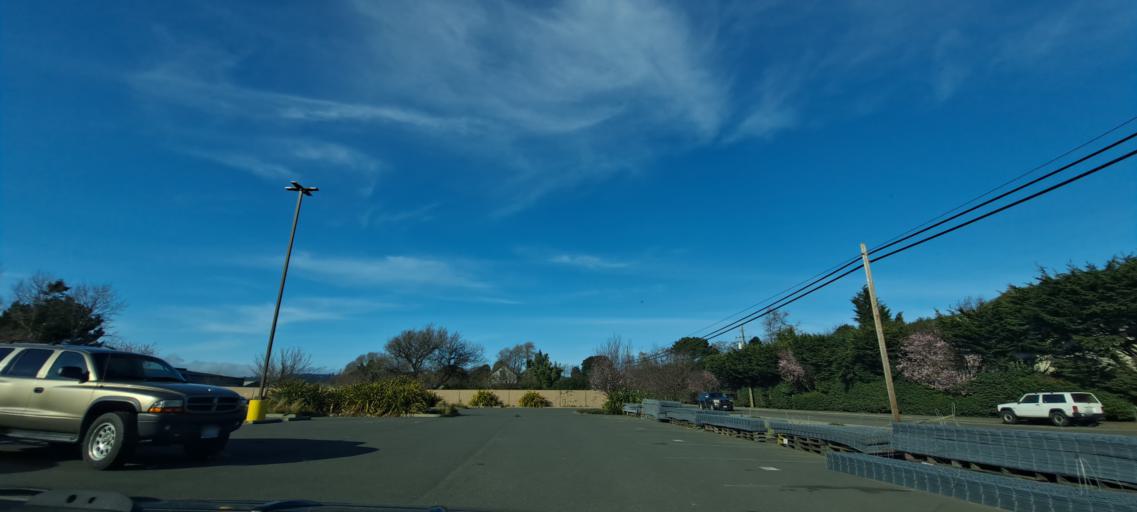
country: US
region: California
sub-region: Humboldt County
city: Fortuna
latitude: 40.5835
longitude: -124.1550
